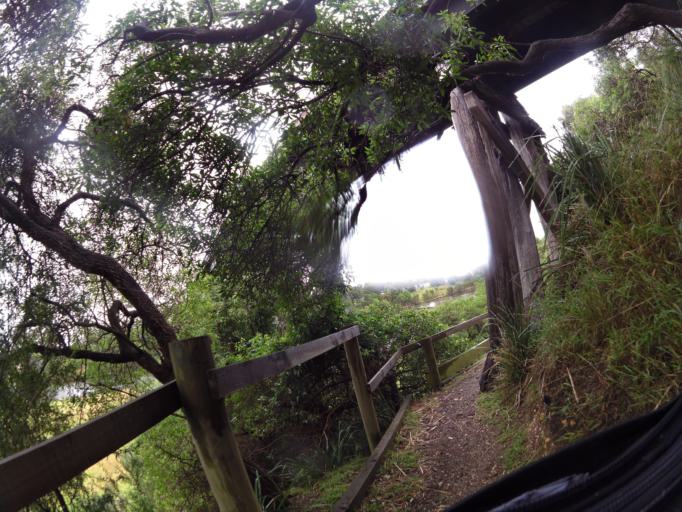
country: AU
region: Victoria
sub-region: East Gippsland
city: Bairnsdale
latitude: -37.8130
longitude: 147.7407
